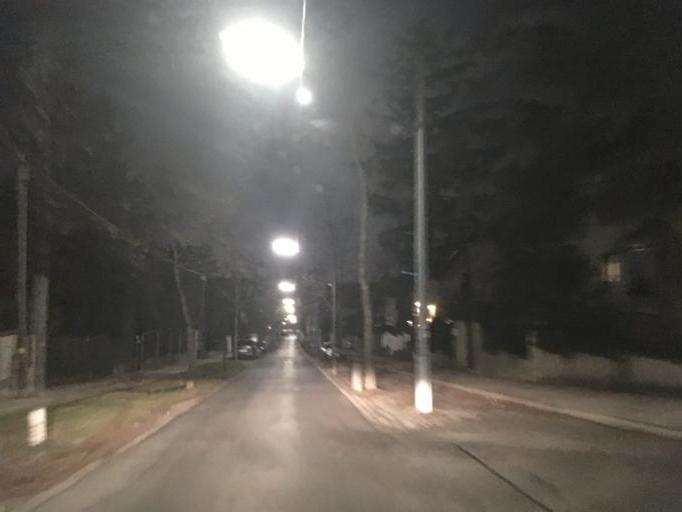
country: AT
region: Vienna
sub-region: Wien Stadt
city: Vienna
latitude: 48.2156
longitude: 16.2892
